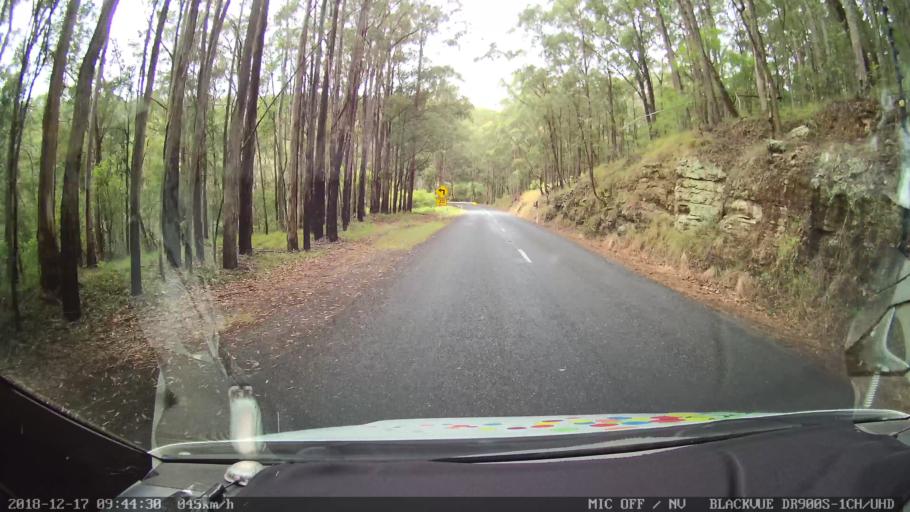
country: AU
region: New South Wales
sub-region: Tenterfield Municipality
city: Carrolls Creek
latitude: -28.9264
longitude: 152.3245
